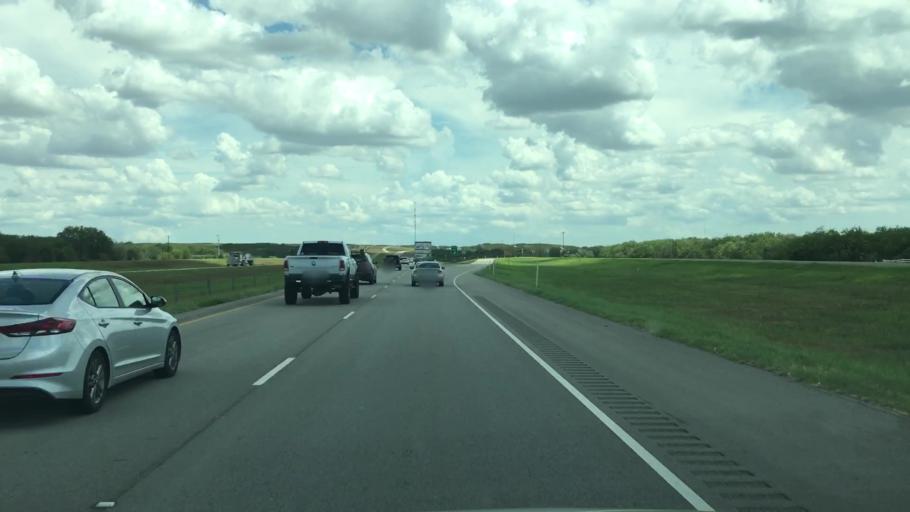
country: US
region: Texas
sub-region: Live Oak County
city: George West
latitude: 28.2662
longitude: -97.9389
